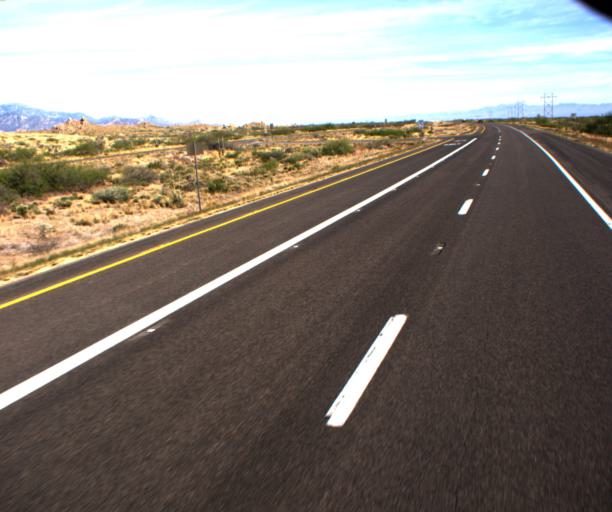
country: US
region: Arizona
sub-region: Graham County
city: Swift Trail Junction
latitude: 32.5218
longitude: -109.6734
